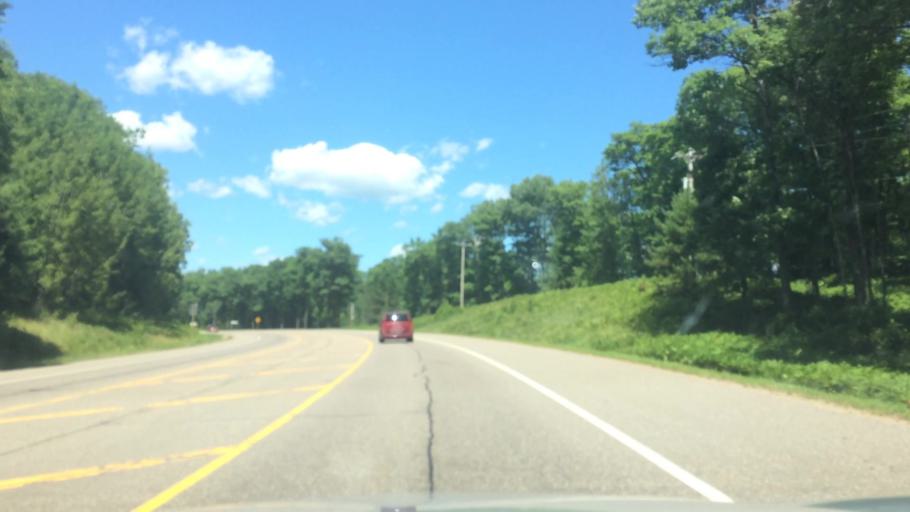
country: US
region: Wisconsin
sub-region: Vilas County
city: Lac du Flambeau
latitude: 45.7874
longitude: -89.7103
